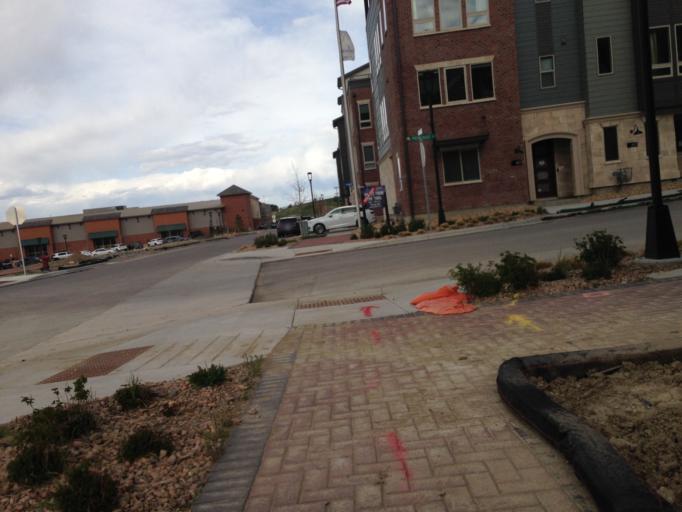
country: US
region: Colorado
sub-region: Boulder County
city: Superior
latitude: 39.9509
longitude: -105.1608
